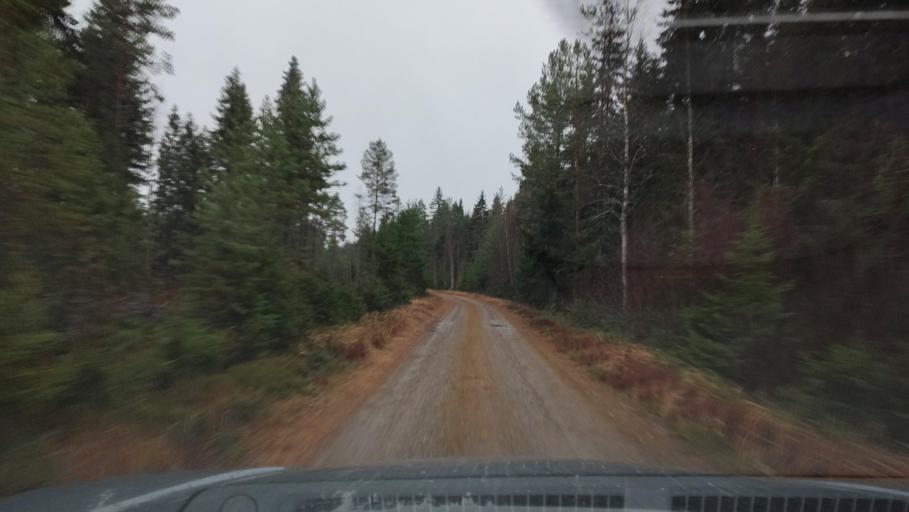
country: FI
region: Southern Ostrobothnia
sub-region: Suupohja
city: Karijoki
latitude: 62.1579
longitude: 21.5897
